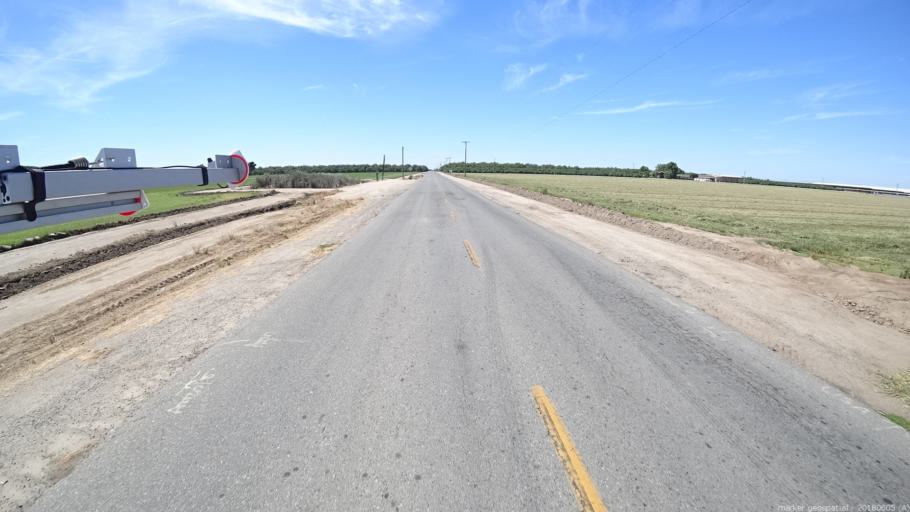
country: US
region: California
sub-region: Madera County
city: Chowchilla
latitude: 37.1116
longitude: -120.3827
